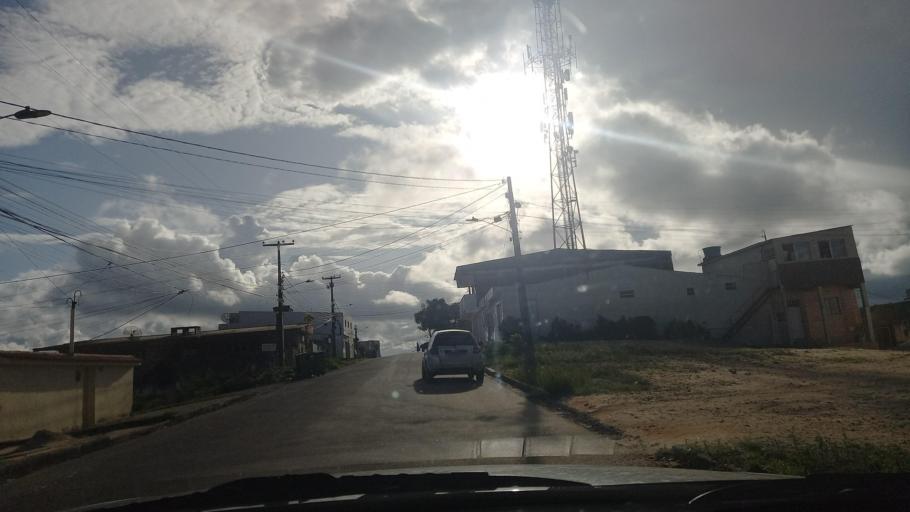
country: BR
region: Pernambuco
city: Garanhuns
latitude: -8.8989
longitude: -36.4968
